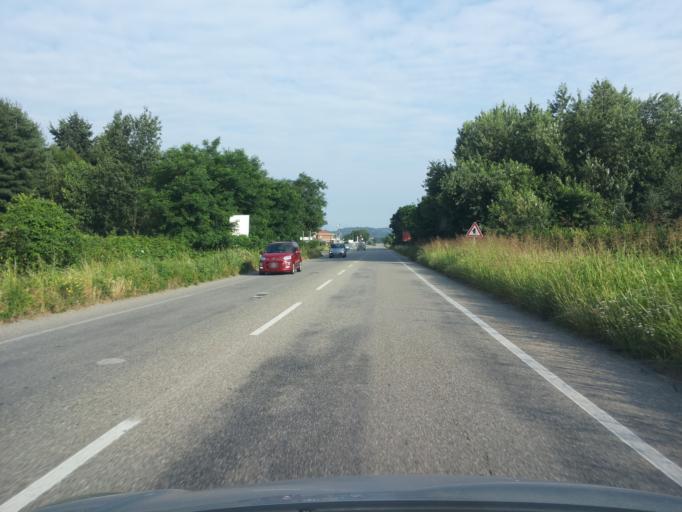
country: IT
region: Piedmont
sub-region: Provincia di Biella
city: Cavaglia
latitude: 45.3915
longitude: 8.1258
